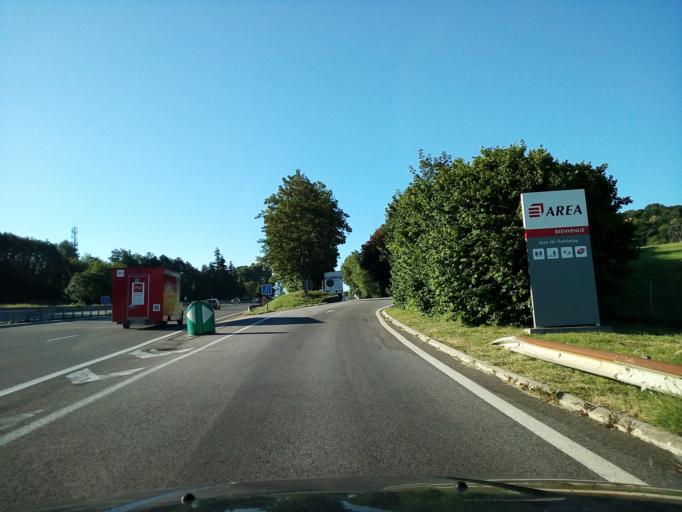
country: FR
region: Rhone-Alpes
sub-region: Departement de l'Isere
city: Saint-Victor-de-Cessieu
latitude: 45.5317
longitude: 5.4076
